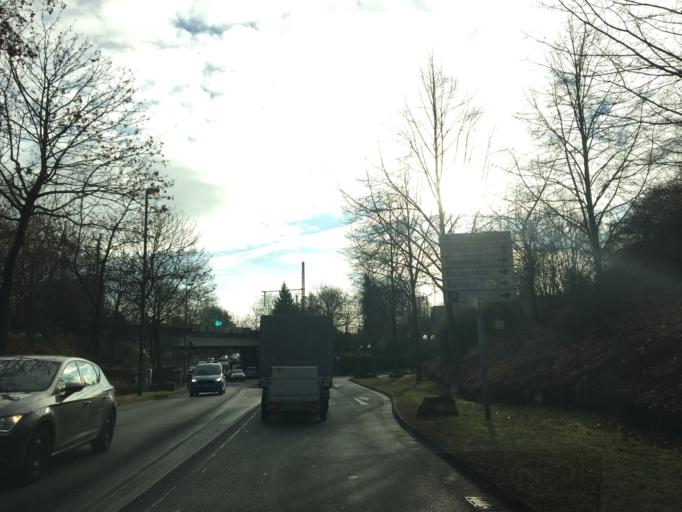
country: DE
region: North Rhine-Westphalia
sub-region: Regierungsbezirk Koln
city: Bonn
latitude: 50.7424
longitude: 7.1251
